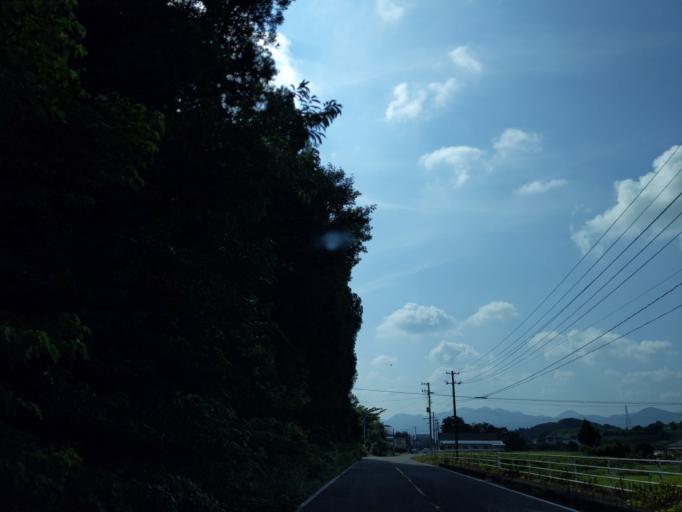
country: JP
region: Fukushima
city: Sukagawa
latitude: 37.3138
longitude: 140.2975
